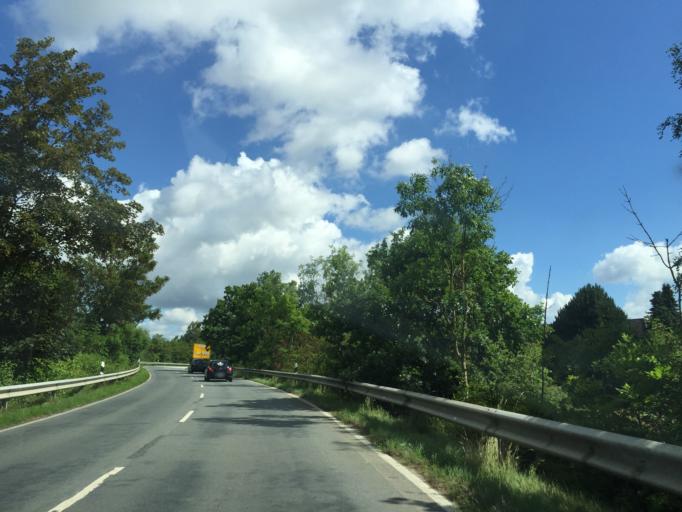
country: DE
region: Schleswig-Holstein
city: Scharbeutz
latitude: 54.0211
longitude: 10.7449
